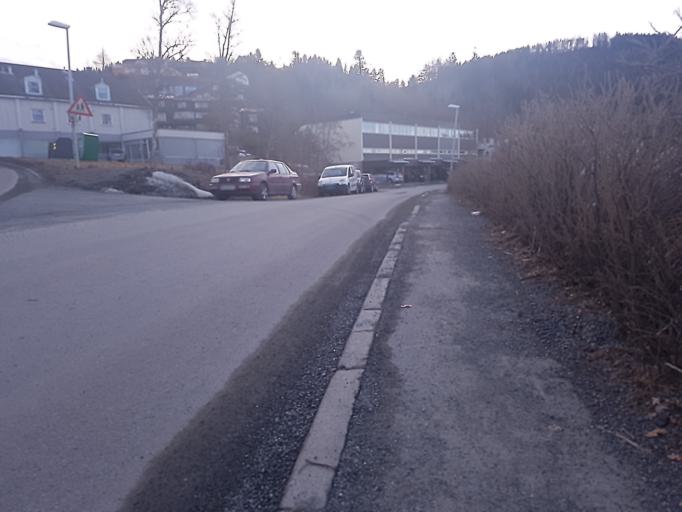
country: NO
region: Sor-Trondelag
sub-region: Trondheim
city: Trondheim
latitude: 63.4275
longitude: 10.3507
